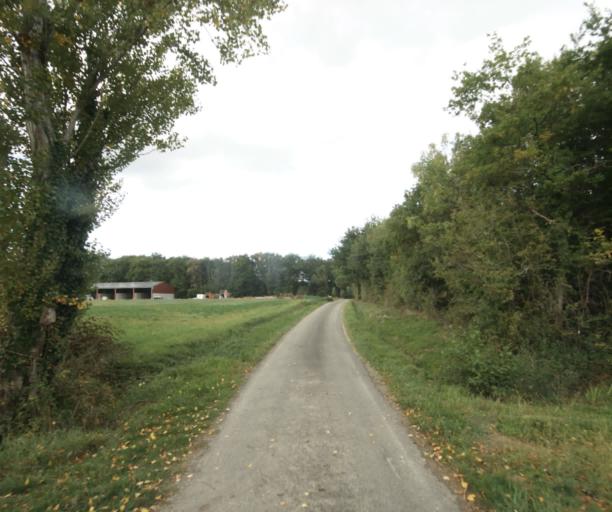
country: FR
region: Midi-Pyrenees
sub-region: Departement du Gers
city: Gondrin
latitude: 43.8590
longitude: 0.2211
